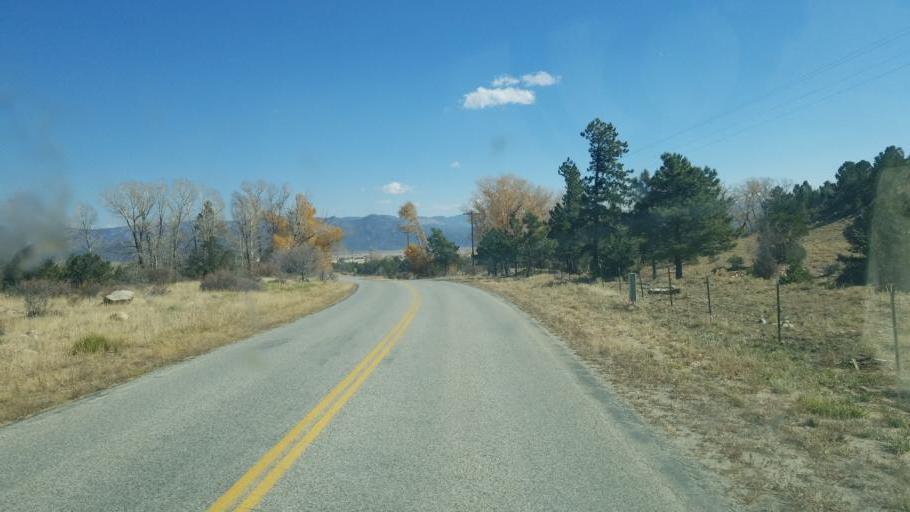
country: US
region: Colorado
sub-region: Chaffee County
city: Buena Vista
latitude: 38.8123
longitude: -106.2102
